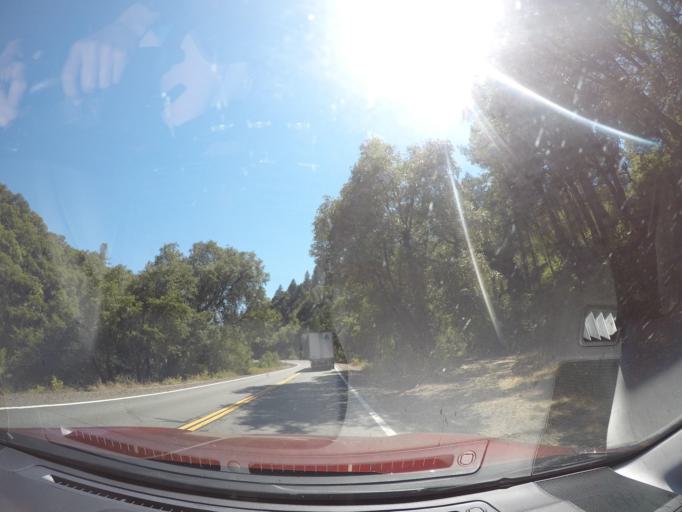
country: US
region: California
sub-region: Shasta County
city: Bella Vista
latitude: 40.7368
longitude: -122.0733
